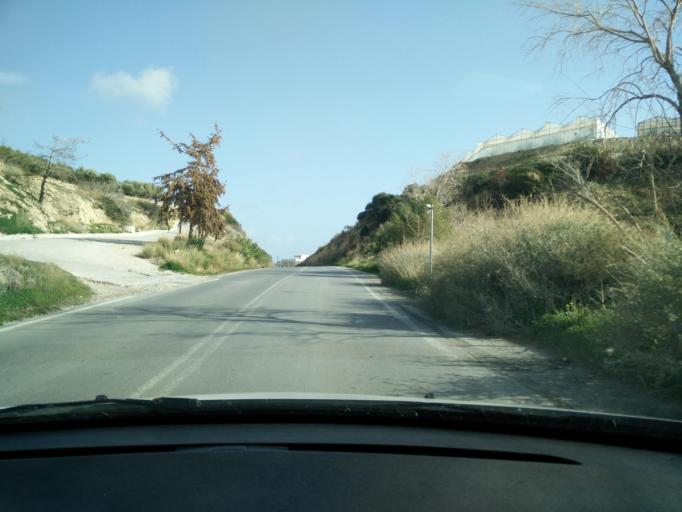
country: GR
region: Crete
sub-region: Nomos Lasithiou
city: Gra Liyia
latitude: 35.0079
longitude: 25.6350
